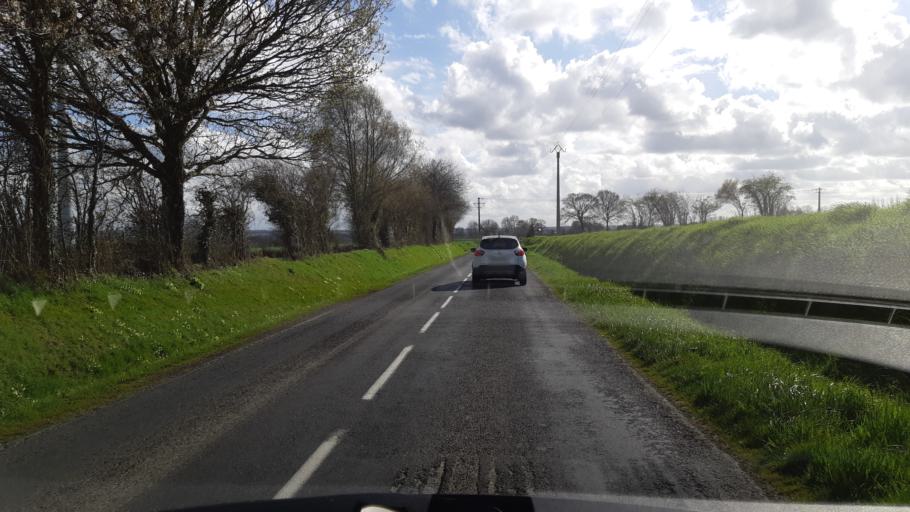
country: FR
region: Lower Normandy
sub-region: Departement de la Manche
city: Percy
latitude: 49.0206
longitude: -1.1606
